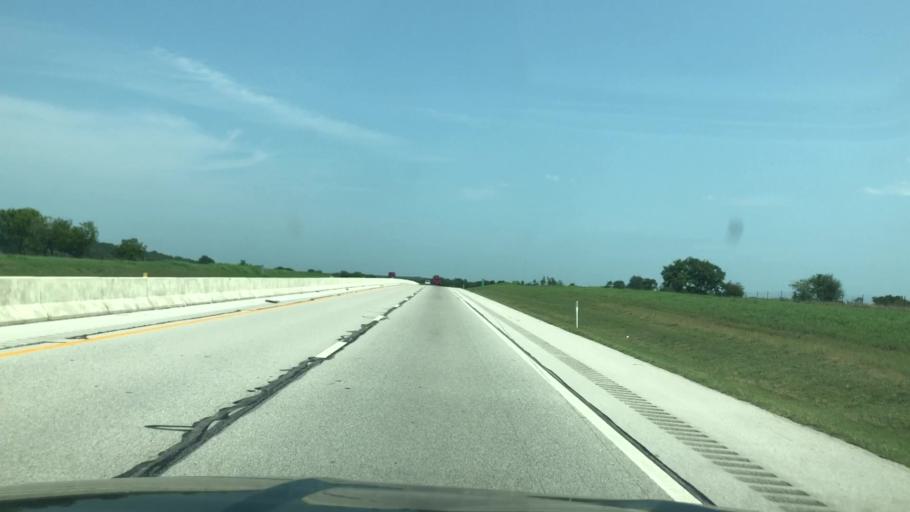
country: US
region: Oklahoma
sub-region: Rogers County
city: Justice
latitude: 36.3441
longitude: -95.4854
